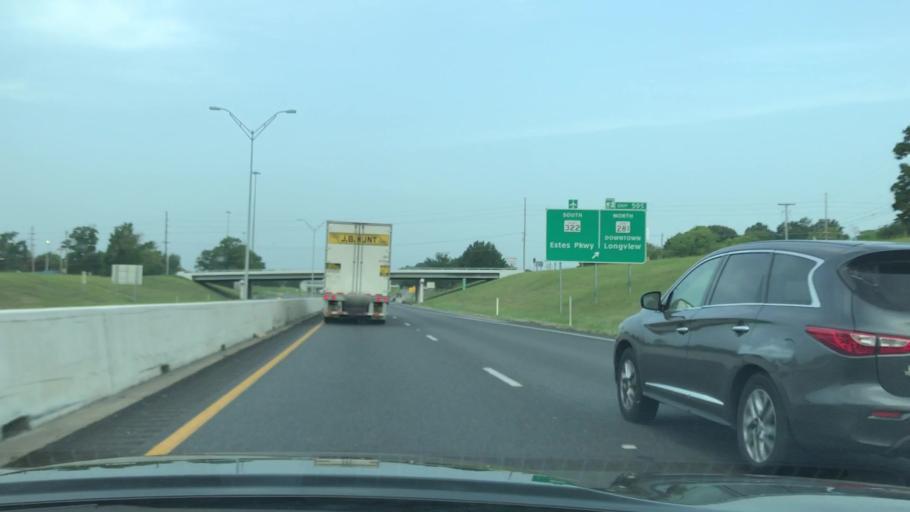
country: US
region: Texas
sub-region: Gregg County
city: Longview
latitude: 32.4483
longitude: -94.7144
